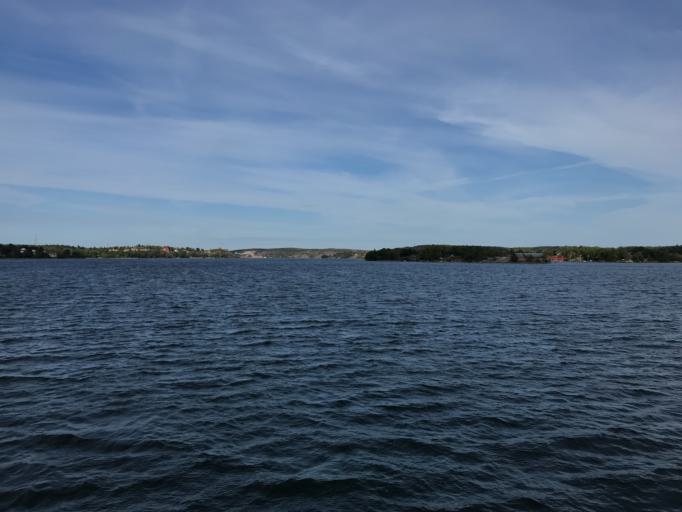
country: SE
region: Stockholm
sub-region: Nacka Kommun
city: Nacka
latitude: 59.3319
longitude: 18.1560
